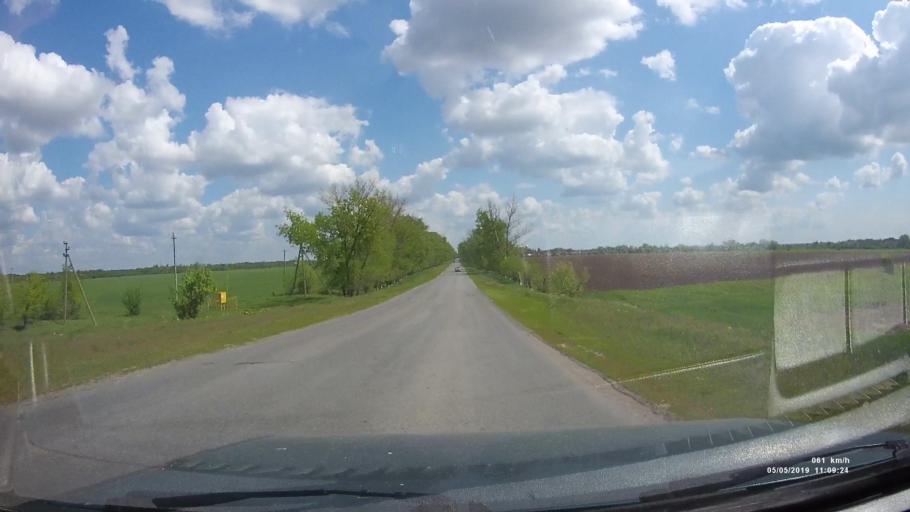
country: RU
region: Rostov
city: Ust'-Donetskiy
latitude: 47.7405
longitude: 40.9242
